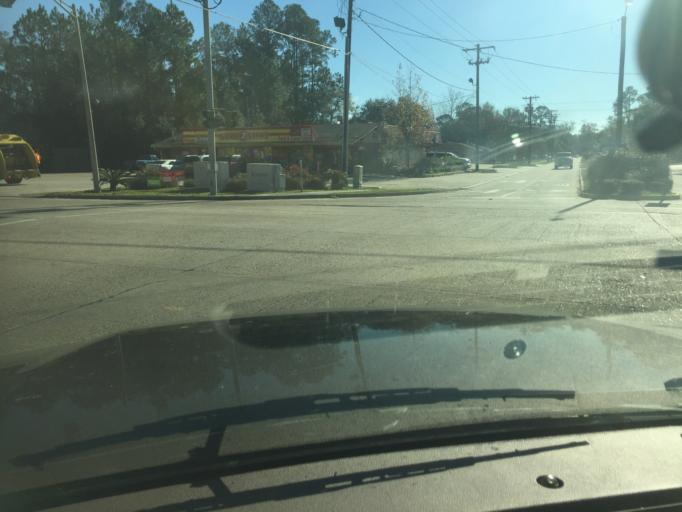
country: US
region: Louisiana
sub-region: Saint Tammany Parish
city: Slidell
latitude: 30.2981
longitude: -89.7606
